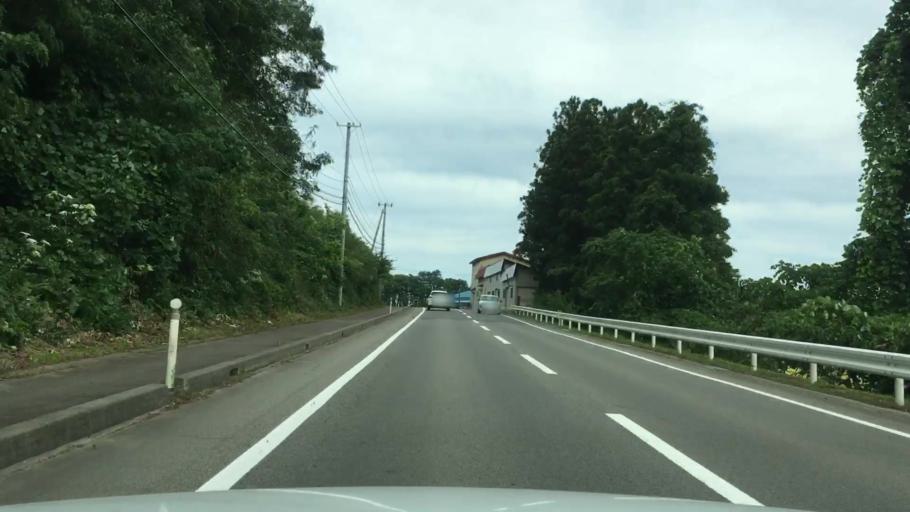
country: JP
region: Aomori
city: Shimokizukuri
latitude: 40.7647
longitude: 140.2247
